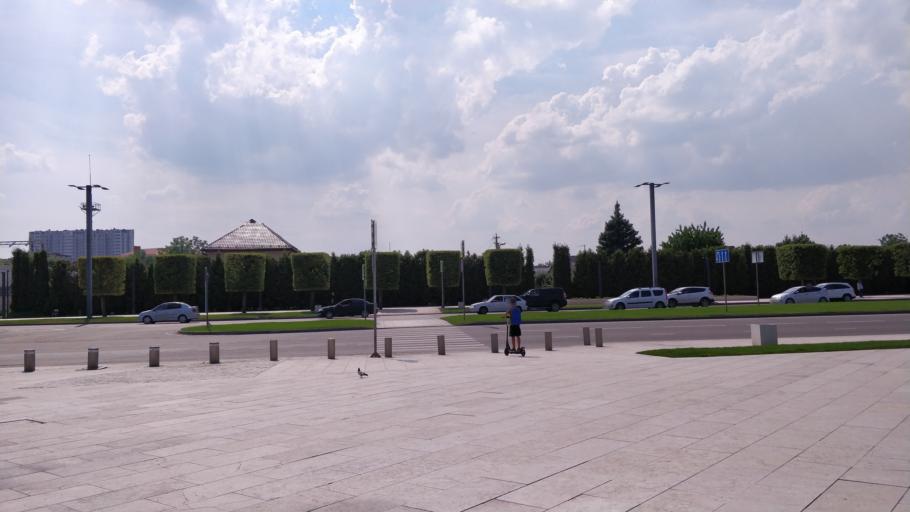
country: RU
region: Krasnodarskiy
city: Krasnodar
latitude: 45.0427
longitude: 39.0276
